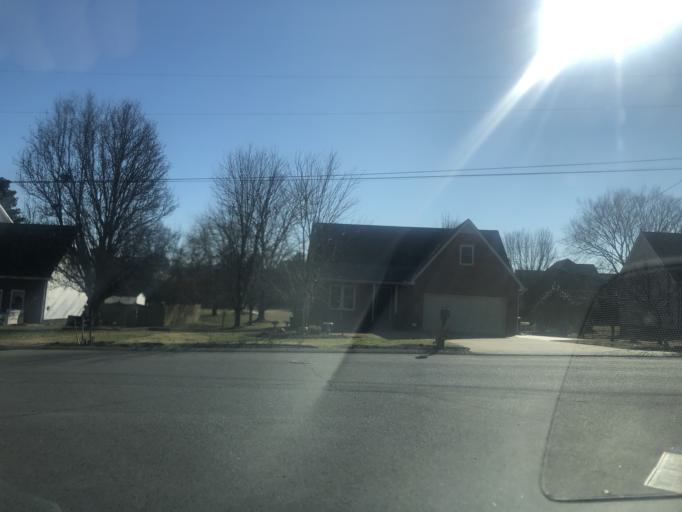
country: US
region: Tennessee
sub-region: Rutherford County
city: Smyrna
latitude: 35.9768
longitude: -86.5397
